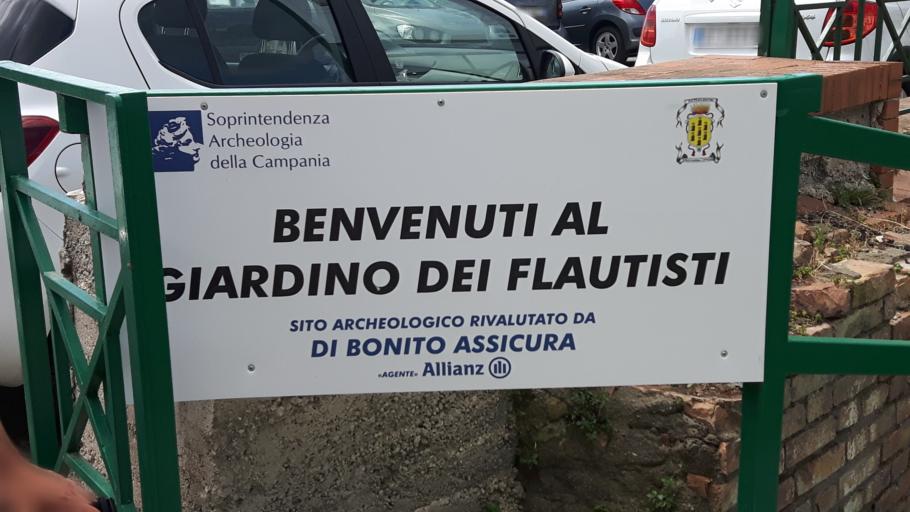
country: IT
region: Campania
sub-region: Provincia di Napoli
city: Pozzuoli
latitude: 40.8225
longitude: 14.1232
